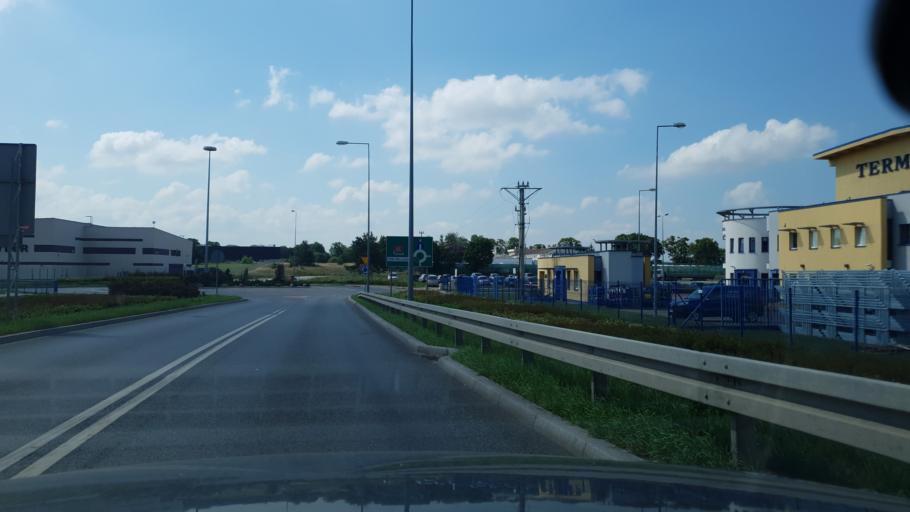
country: PL
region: Kujawsko-Pomorskie
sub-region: Grudziadz
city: Grudziadz
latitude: 53.4390
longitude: 18.7162
